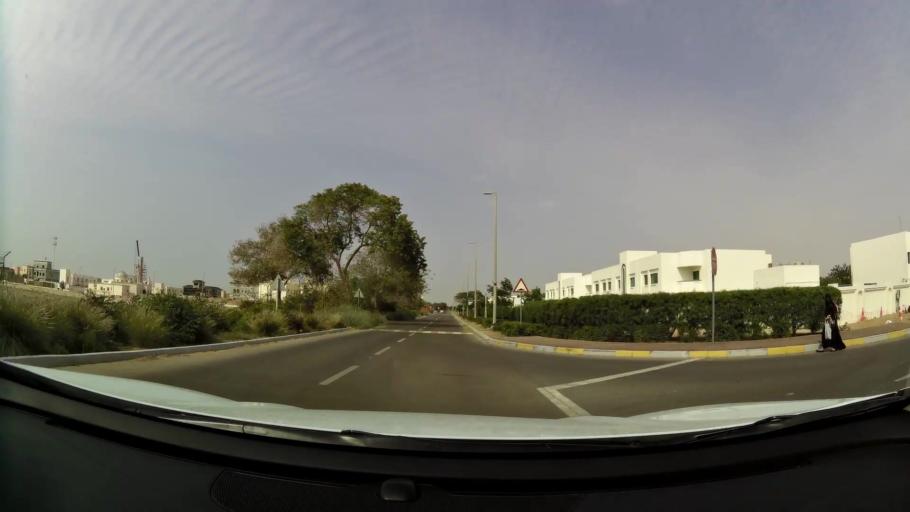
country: AE
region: Abu Dhabi
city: Abu Dhabi
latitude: 24.5695
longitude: 54.6931
